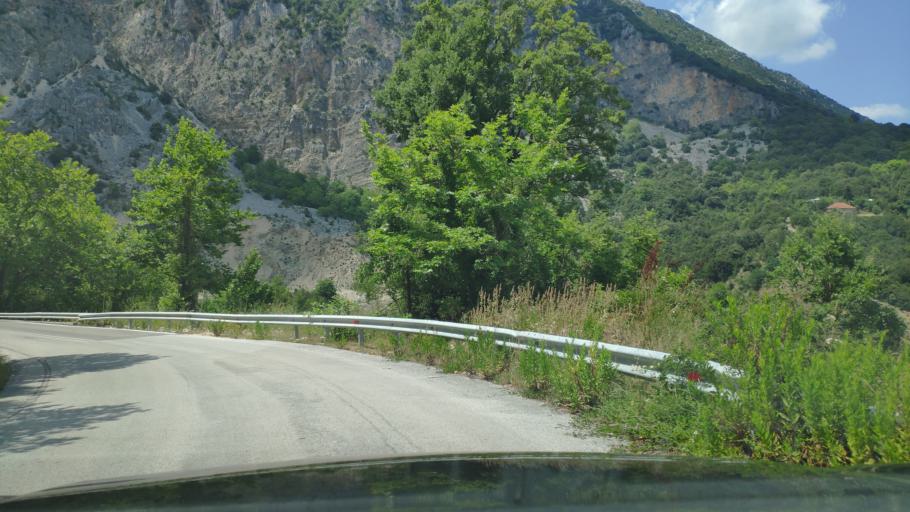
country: GR
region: Epirus
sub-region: Nomos Artas
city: Agios Dimitrios
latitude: 39.3436
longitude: 21.0068
